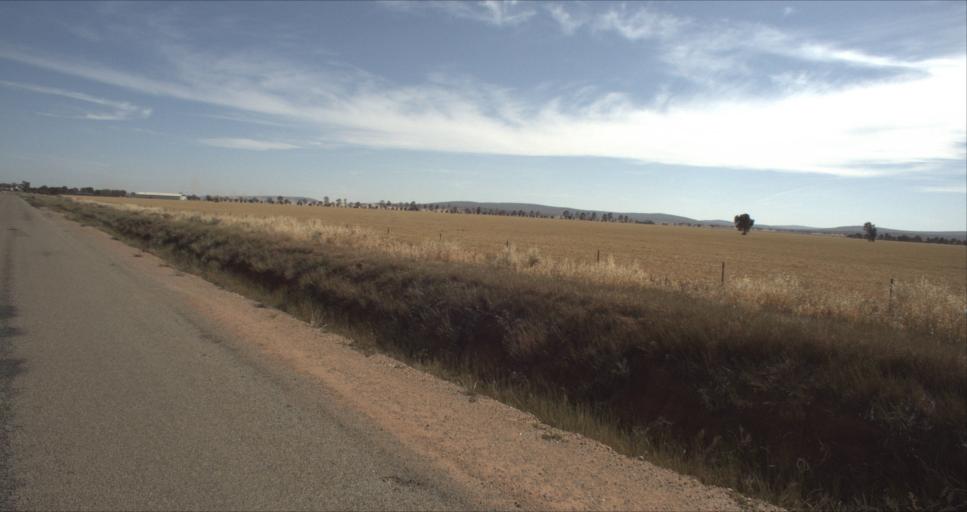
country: AU
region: New South Wales
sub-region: Leeton
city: Leeton
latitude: -34.5699
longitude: 146.4737
